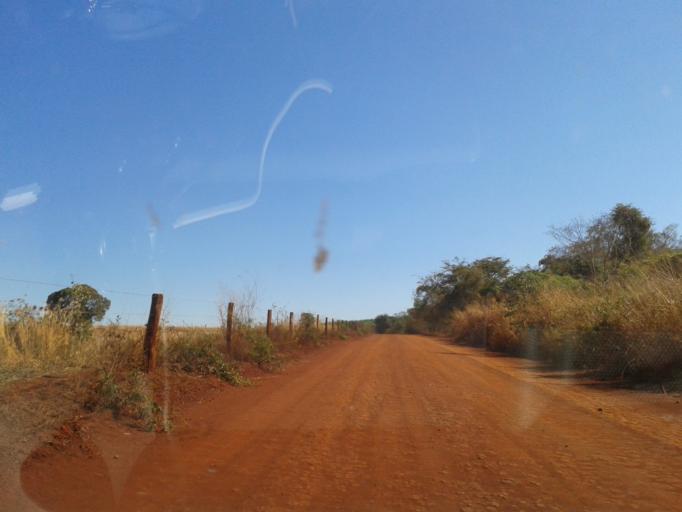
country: BR
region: Minas Gerais
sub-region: Centralina
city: Centralina
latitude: -18.5775
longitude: -49.1335
